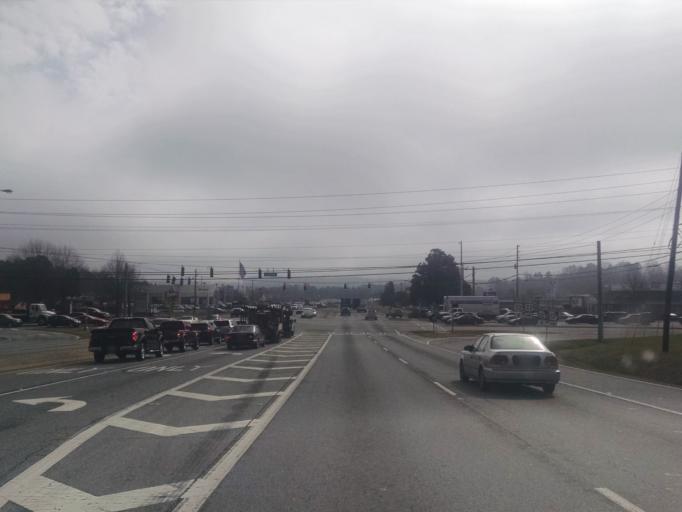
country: US
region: Georgia
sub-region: Gwinnett County
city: Sugar Hill
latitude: 34.0966
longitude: -84.0139
